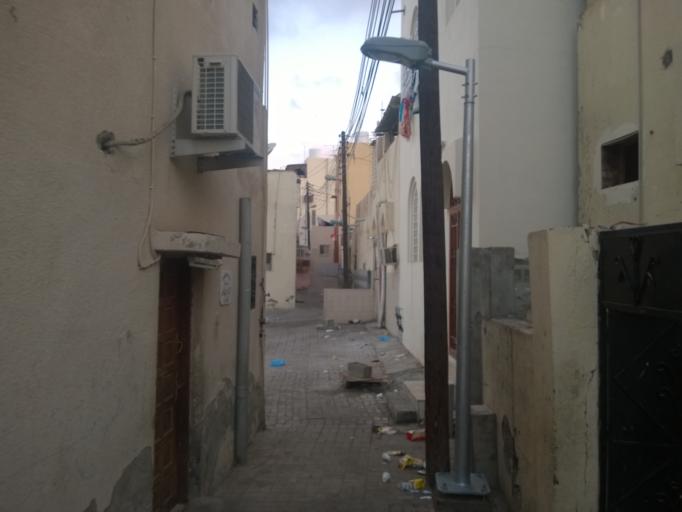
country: OM
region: Muhafazat Masqat
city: Muscat
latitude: 23.6218
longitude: 58.5599
